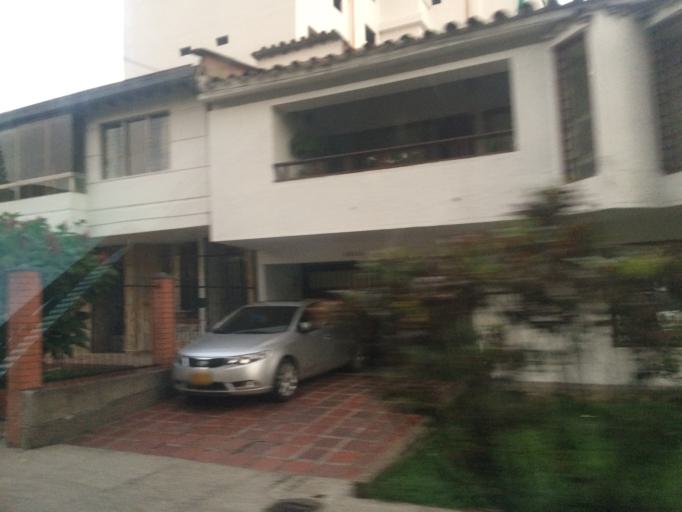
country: CO
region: Antioquia
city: Medellin
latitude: 6.2522
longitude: -75.5866
